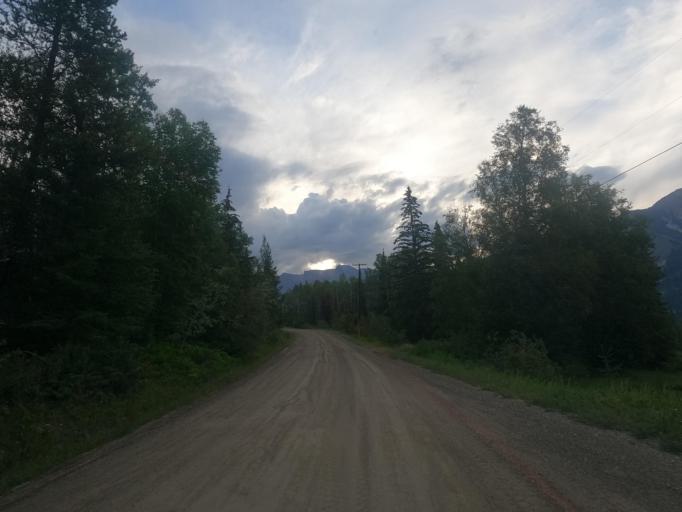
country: CA
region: British Columbia
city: Golden
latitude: 51.4458
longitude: -117.0096
